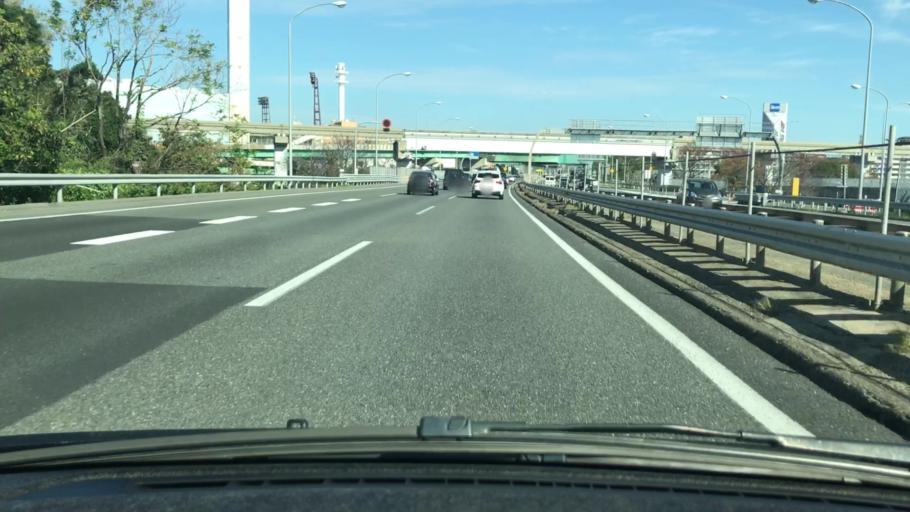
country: JP
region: Osaka
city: Ibaraki
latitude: 34.8062
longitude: 135.5428
